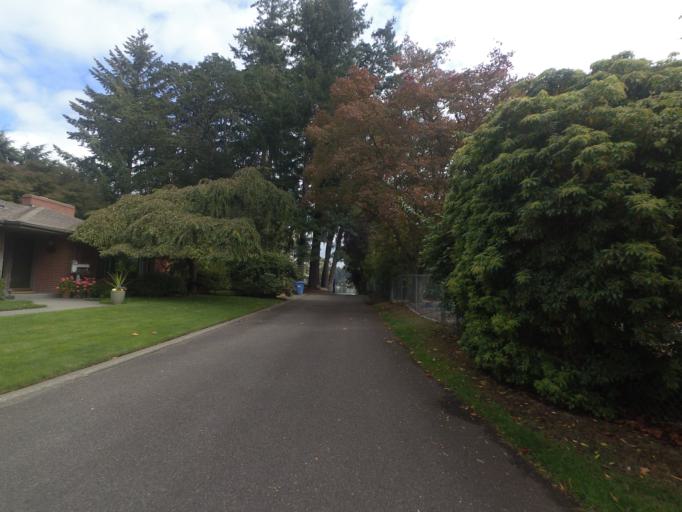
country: US
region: Washington
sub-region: Pierce County
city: Lakewood
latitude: 47.1692
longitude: -122.5449
